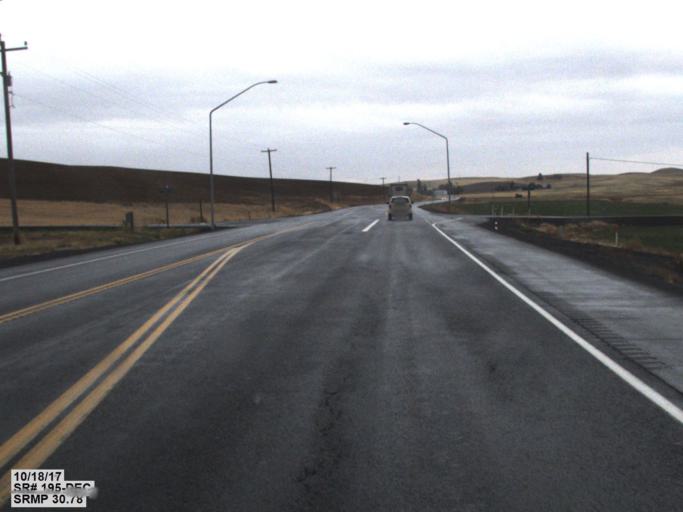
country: US
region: Washington
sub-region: Whitman County
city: Colfax
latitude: 46.7939
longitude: -117.3125
